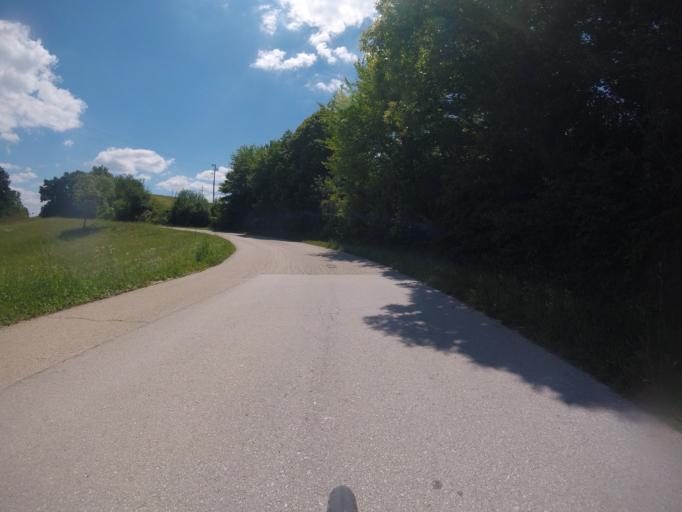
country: HR
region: Karlovacka
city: Ozalj
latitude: 45.6708
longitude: 15.4077
